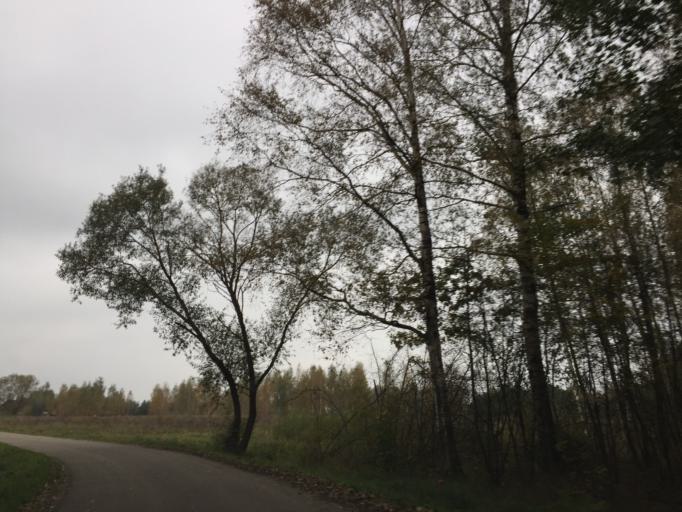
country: LV
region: Jelgava
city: Jelgava
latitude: 56.7335
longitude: 23.6857
